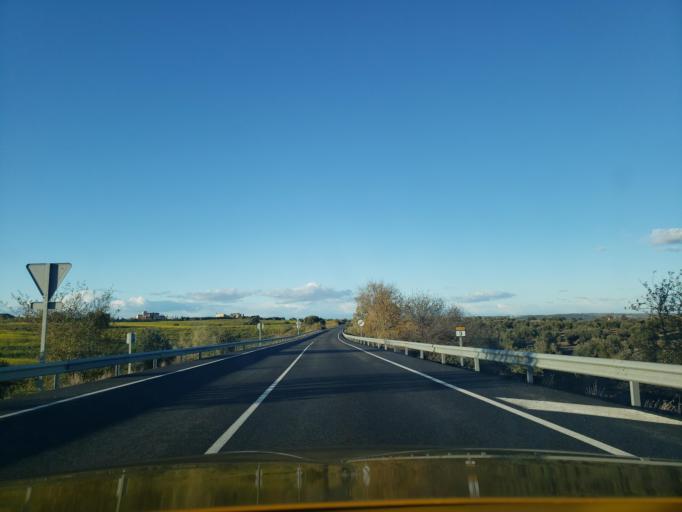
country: ES
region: Castille-La Mancha
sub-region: Province of Toledo
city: Cobisa
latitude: 39.8298
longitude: -4.0182
